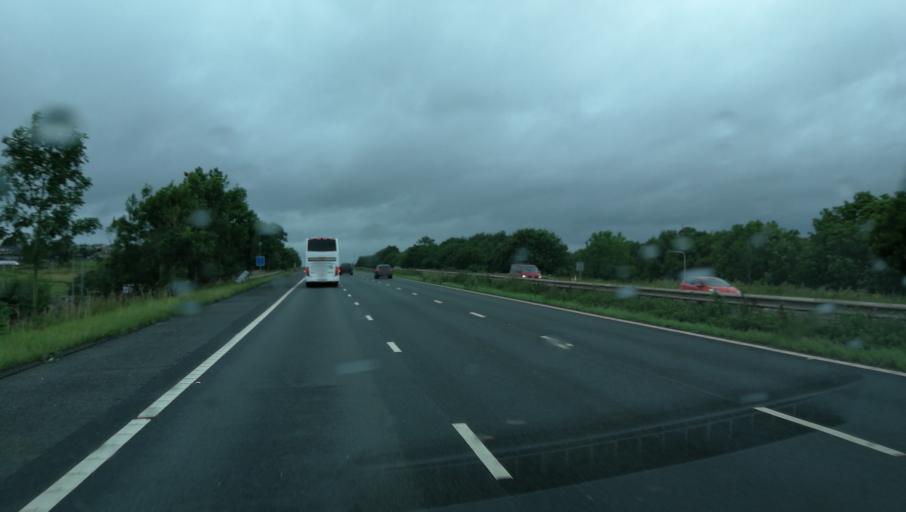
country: GB
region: England
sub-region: Borough of Wigan
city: Atherton
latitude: 53.5545
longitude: -2.4872
